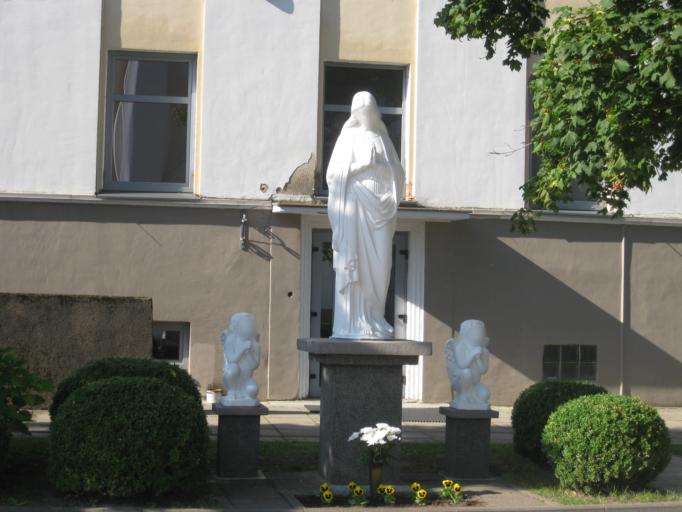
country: LT
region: Vilnius County
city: Ukmerge
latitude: 55.2494
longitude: 24.7621
